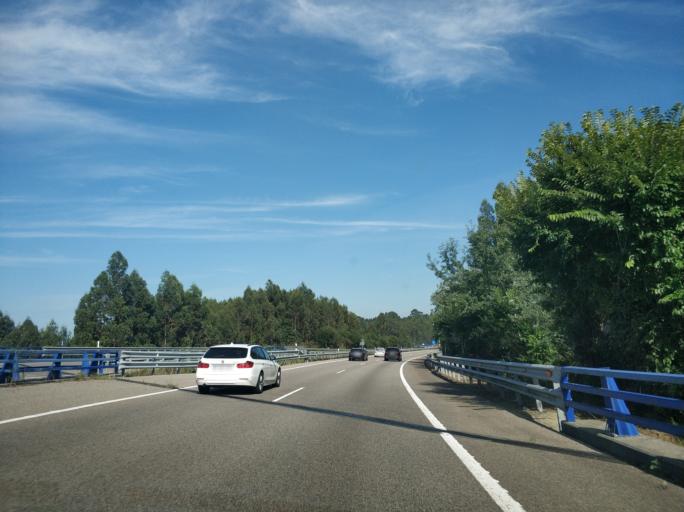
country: ES
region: Asturias
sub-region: Province of Asturias
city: Castrillon
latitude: 43.5455
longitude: -6.0144
